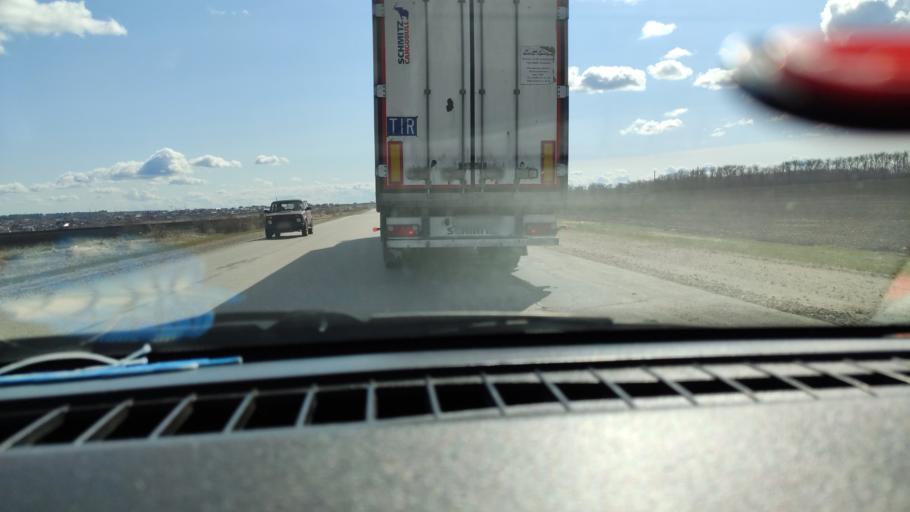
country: RU
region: Samara
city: Varlamovo
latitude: 53.1176
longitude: 48.3405
